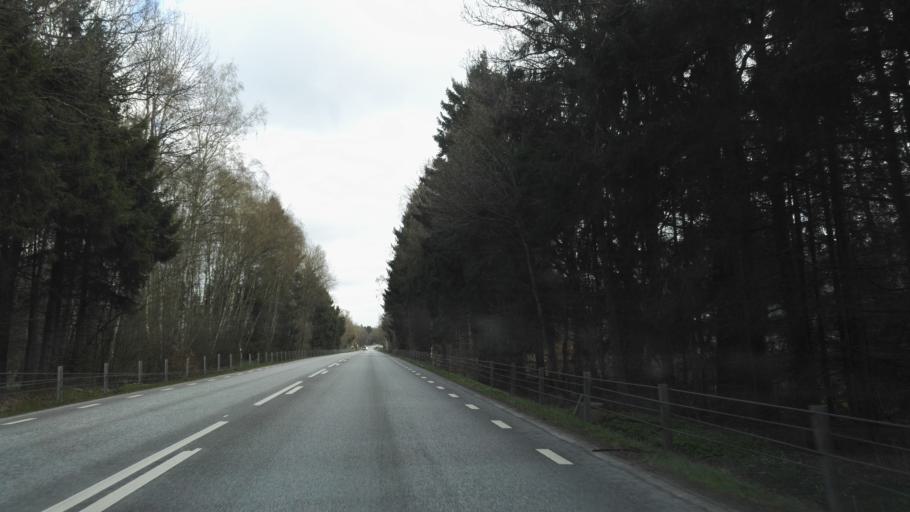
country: SE
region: Skane
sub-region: Hoors Kommun
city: Satofta
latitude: 55.9135
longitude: 13.5977
